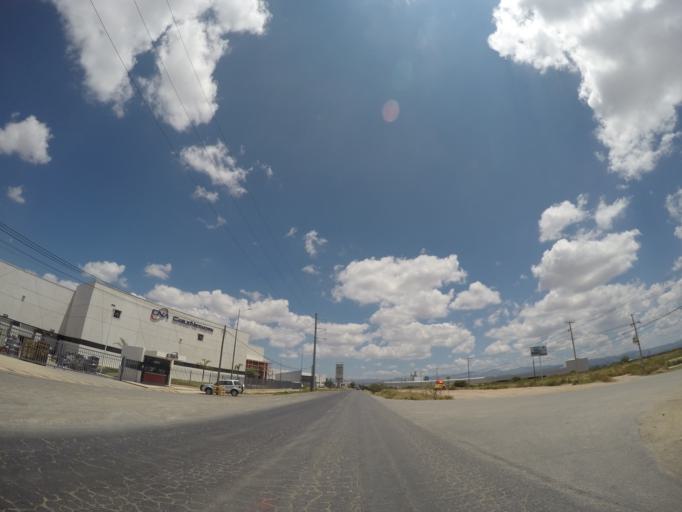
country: MX
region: San Luis Potosi
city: La Pila
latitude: 22.0418
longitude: -100.8853
